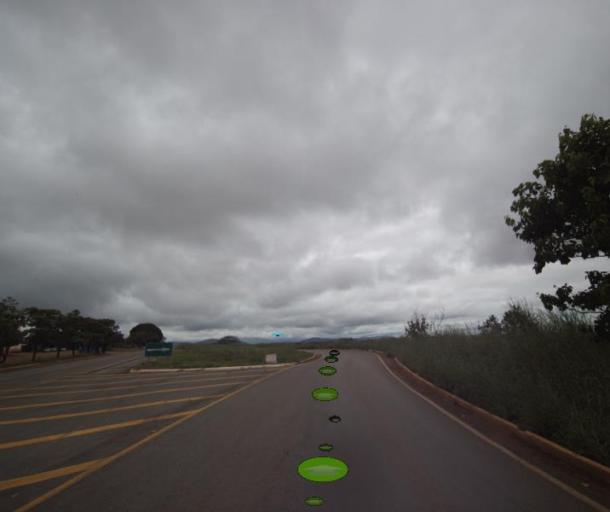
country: BR
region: Goias
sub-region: Barro Alto
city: Barro Alto
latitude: -14.8357
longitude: -49.0324
